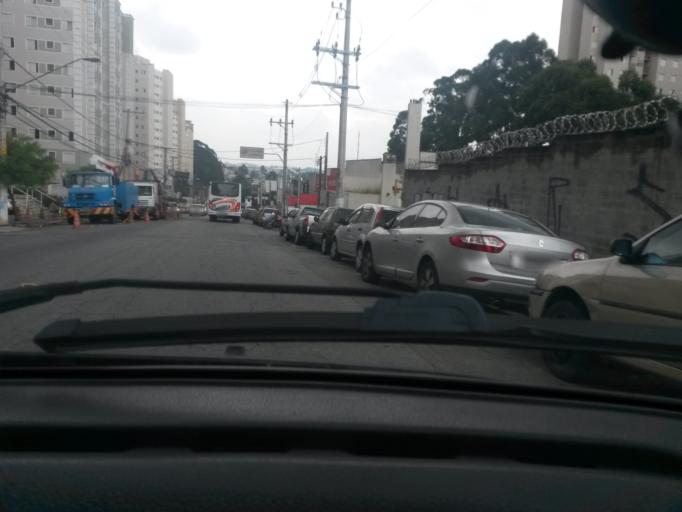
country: BR
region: Sao Paulo
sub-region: Sao Bernardo Do Campo
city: Sao Bernardo do Campo
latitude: -23.7073
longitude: -46.5685
